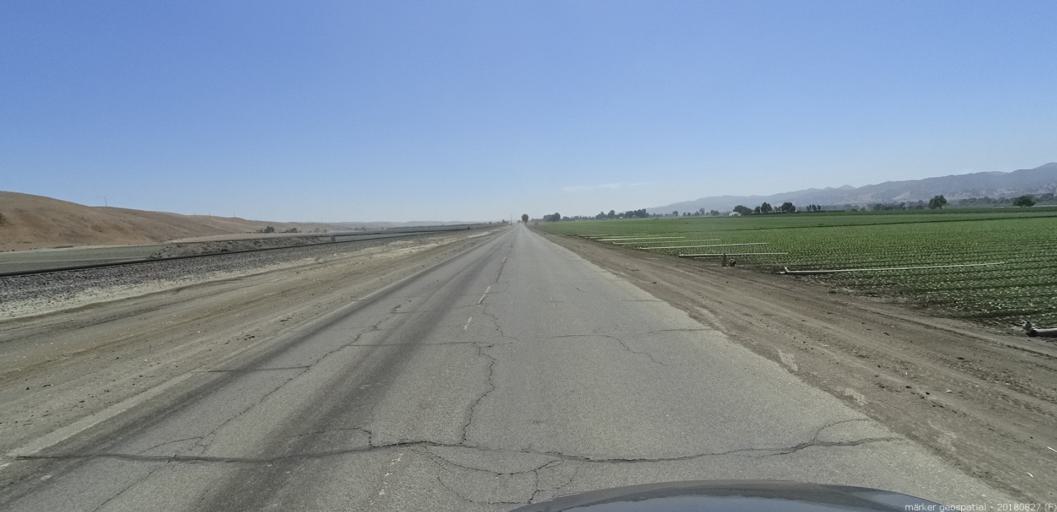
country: US
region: California
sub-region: Monterey County
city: King City
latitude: 36.0409
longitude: -120.9163
